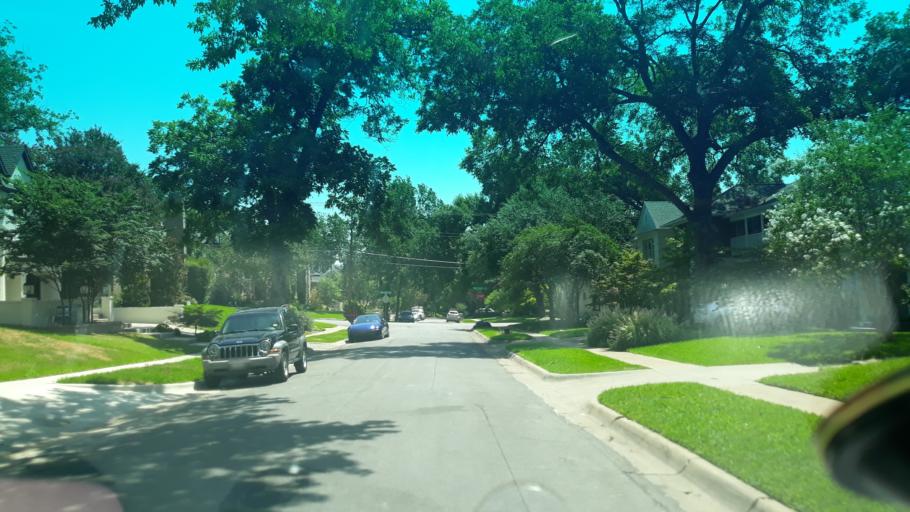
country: US
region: Texas
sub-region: Dallas County
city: Highland Park
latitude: 32.8181
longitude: -96.7381
